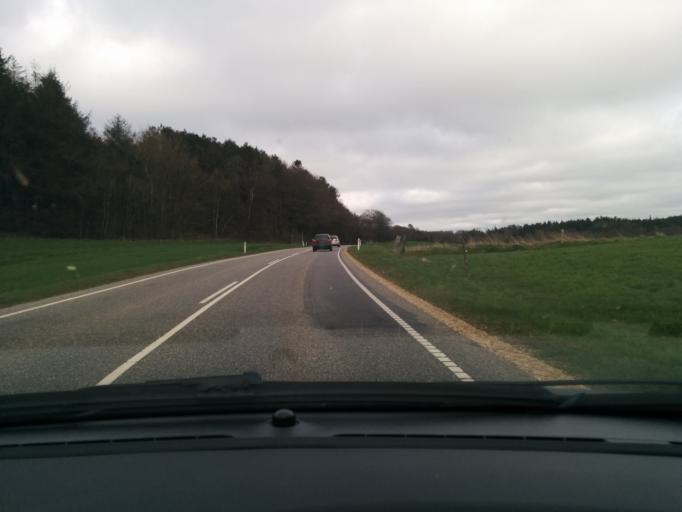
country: DK
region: Central Jutland
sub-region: Favrskov Kommune
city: Hammel
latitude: 56.2152
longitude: 9.7629
